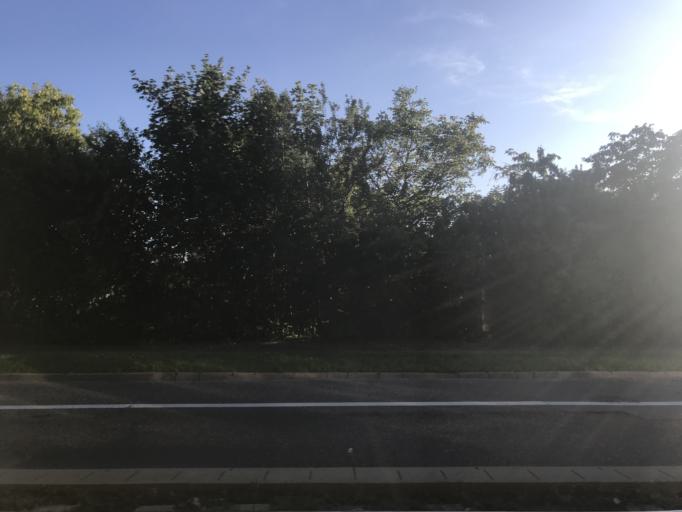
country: PL
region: Pomeranian Voivodeship
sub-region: Sopot
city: Sopot
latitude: 54.3945
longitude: 18.5731
